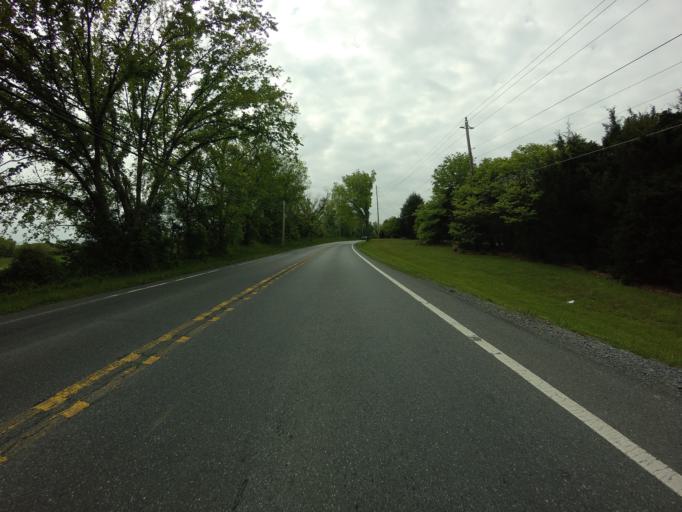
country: US
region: Maryland
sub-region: Frederick County
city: Green Valley
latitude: 39.3109
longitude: -77.3257
